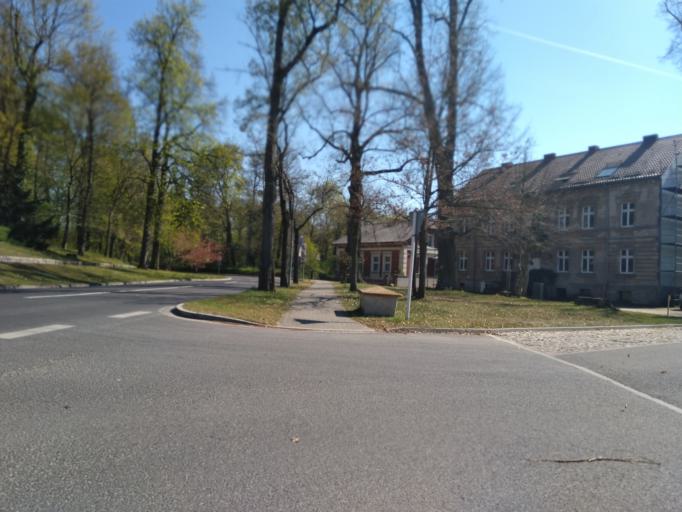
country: DE
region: Brandenburg
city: Biesenthal
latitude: 52.7642
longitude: 13.6455
